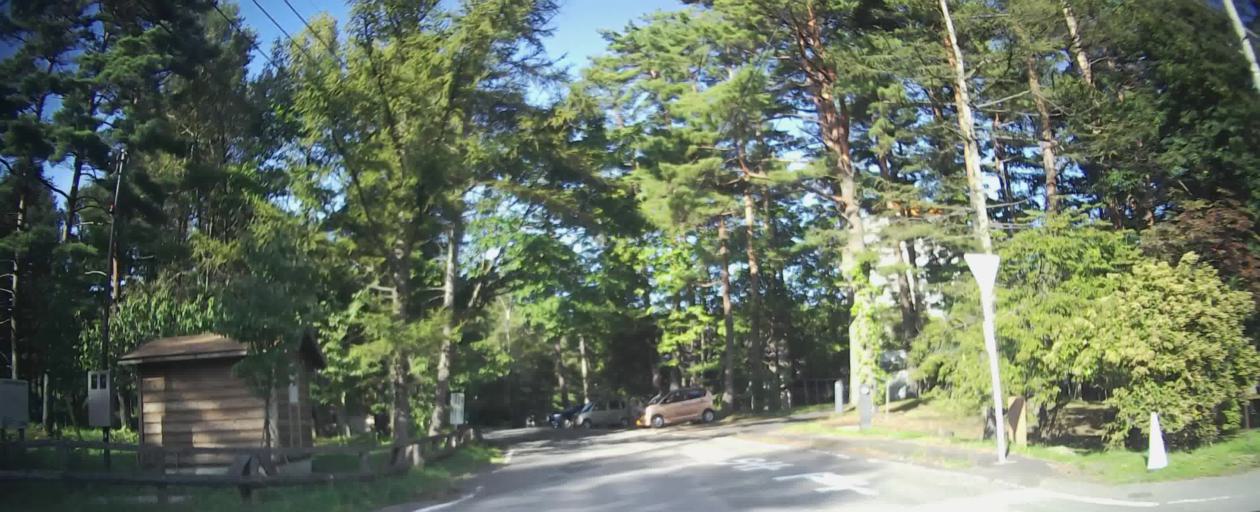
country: JP
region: Gunma
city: Nakanojomachi
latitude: 36.6267
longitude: 138.6021
